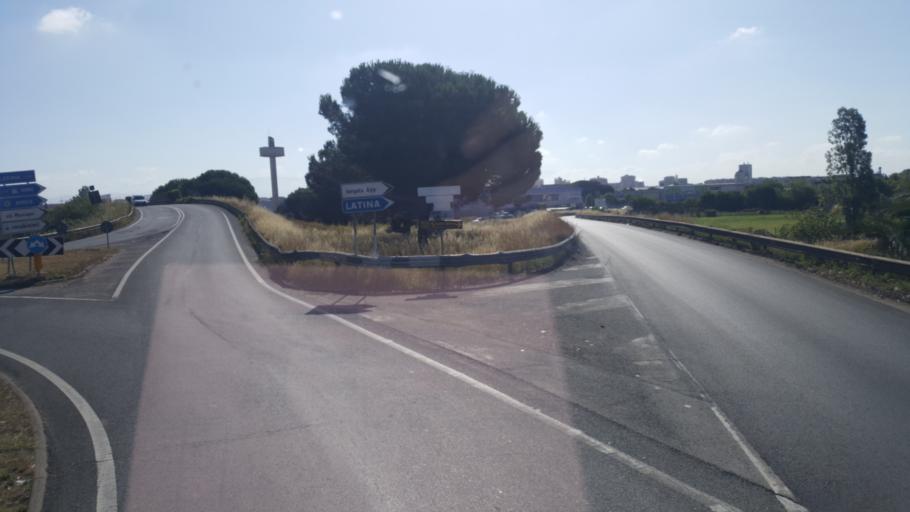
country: IT
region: Latium
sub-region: Provincia di Latina
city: Aprilia
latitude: 41.5781
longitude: 12.6510
